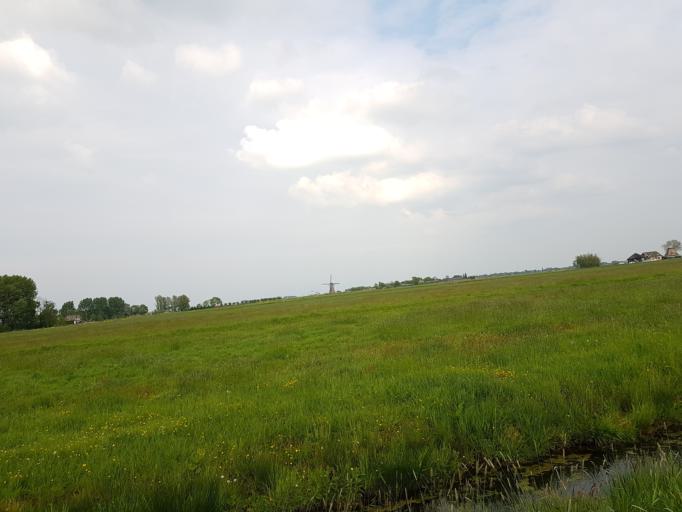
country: NL
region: South Holland
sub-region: Gemeente Vlist
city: Haastrecht
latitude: 51.9916
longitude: 4.7712
